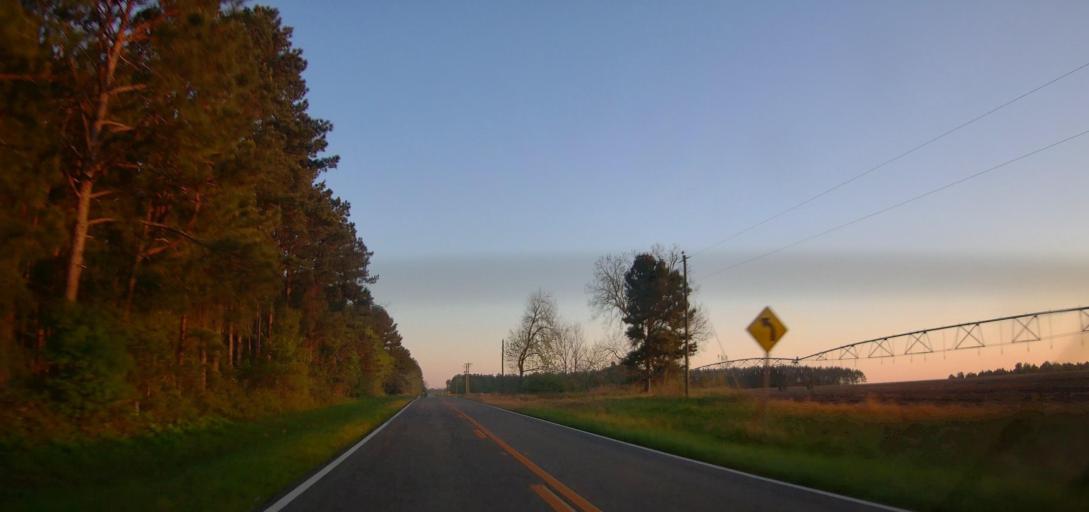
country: US
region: Georgia
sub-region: Ben Hill County
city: Fitzgerald
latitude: 31.7752
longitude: -83.3845
